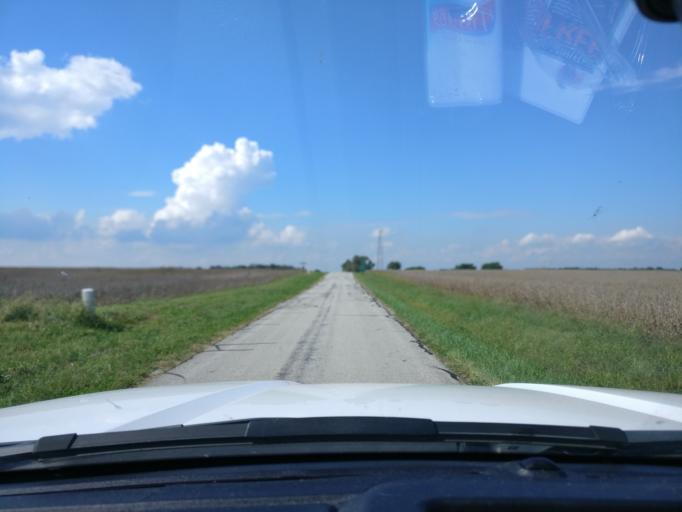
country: US
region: Ohio
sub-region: Warren County
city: Waynesville
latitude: 39.4642
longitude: -83.9859
